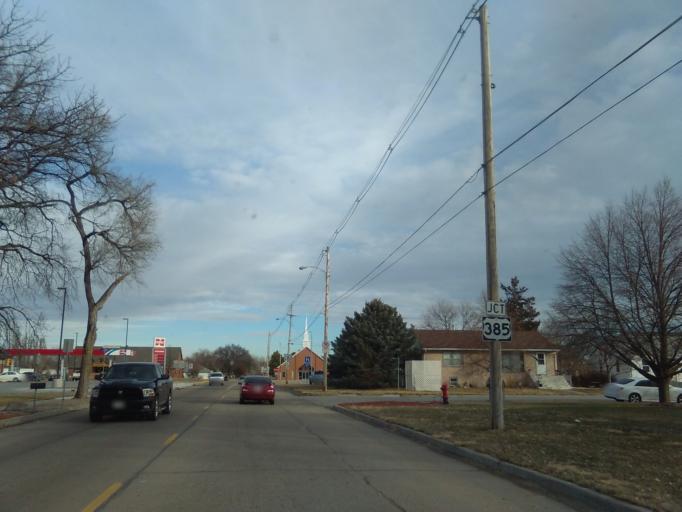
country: US
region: Nebraska
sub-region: Morrill County
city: Bridgeport
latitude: 41.6705
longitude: -103.1015
